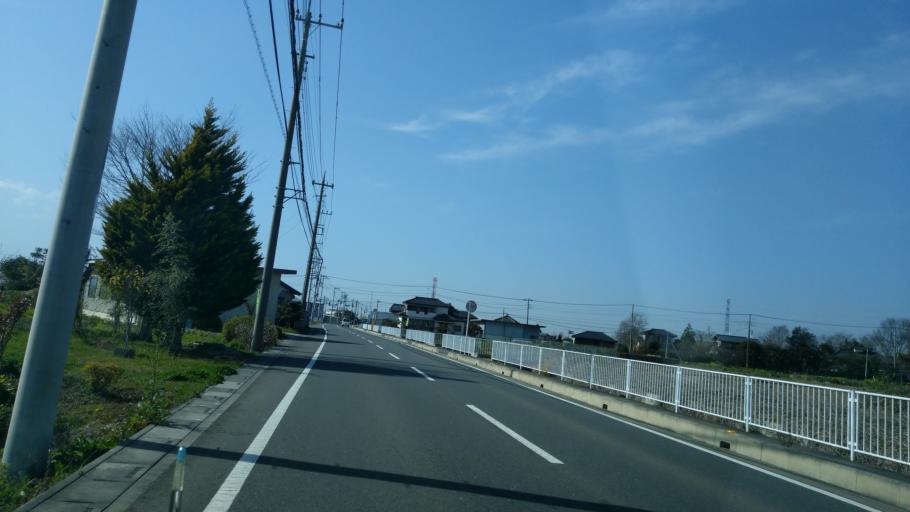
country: JP
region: Saitama
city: Kawagoe
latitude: 35.9804
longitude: 139.4848
